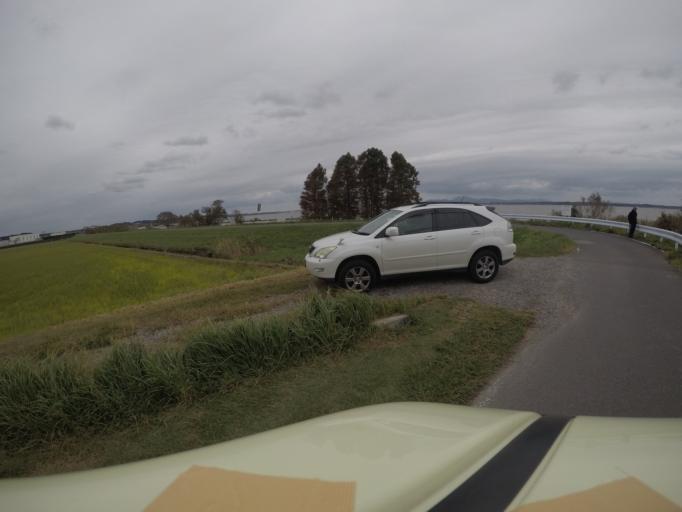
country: JP
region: Ibaraki
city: Inashiki
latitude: 36.0284
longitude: 140.3070
